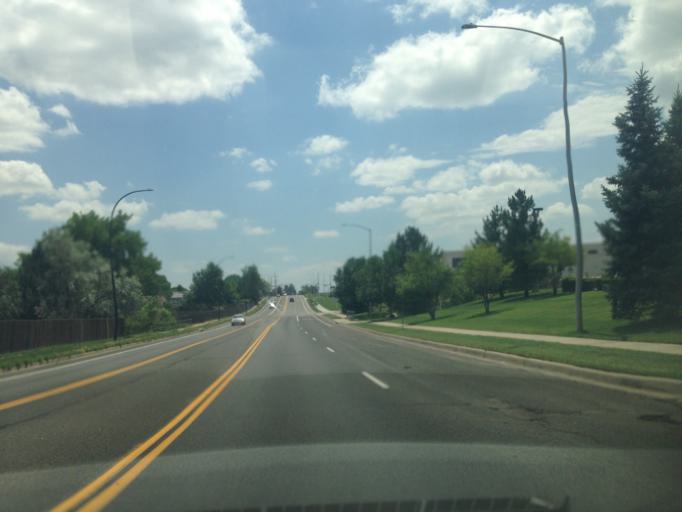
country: US
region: Colorado
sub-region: Broomfield County
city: Broomfield
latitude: 39.9056
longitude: -105.0718
